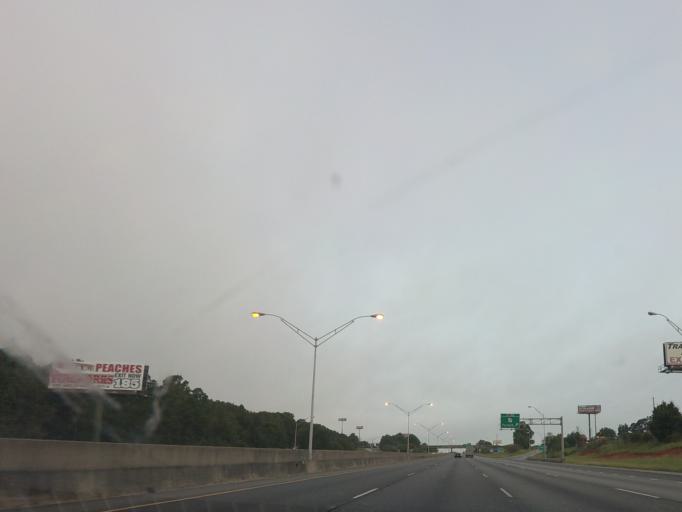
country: US
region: Georgia
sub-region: Monroe County
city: Forsyth
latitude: 33.0257
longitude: -83.9053
